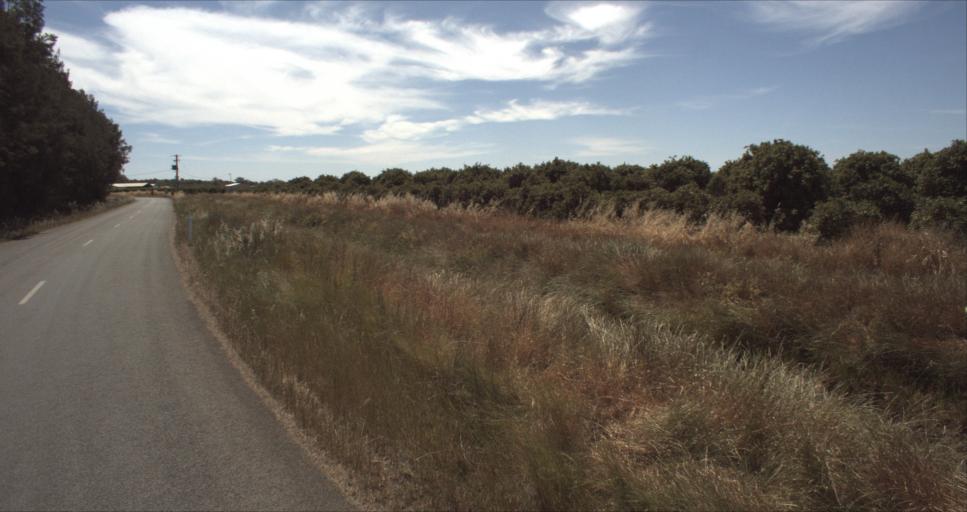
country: AU
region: New South Wales
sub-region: Leeton
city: Leeton
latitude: -34.5931
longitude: 146.4675
